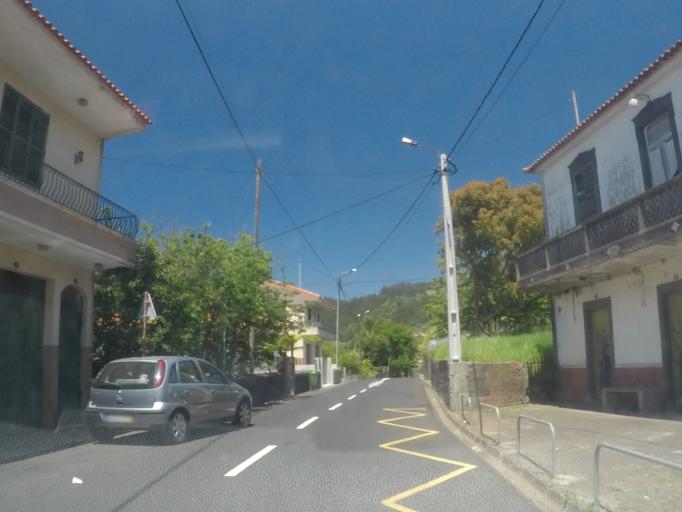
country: PT
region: Madeira
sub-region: Camara de Lobos
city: Curral das Freiras
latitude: 32.6854
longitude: -16.9910
